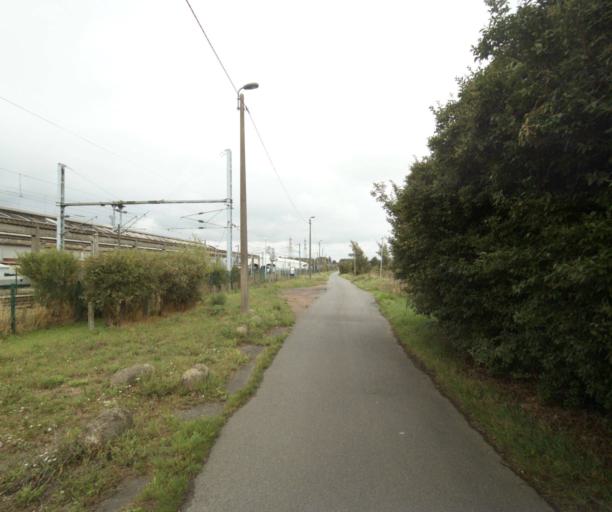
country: FR
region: Nord-Pas-de-Calais
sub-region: Departement du Nord
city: Lezennes
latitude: 50.6224
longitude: 3.1140
